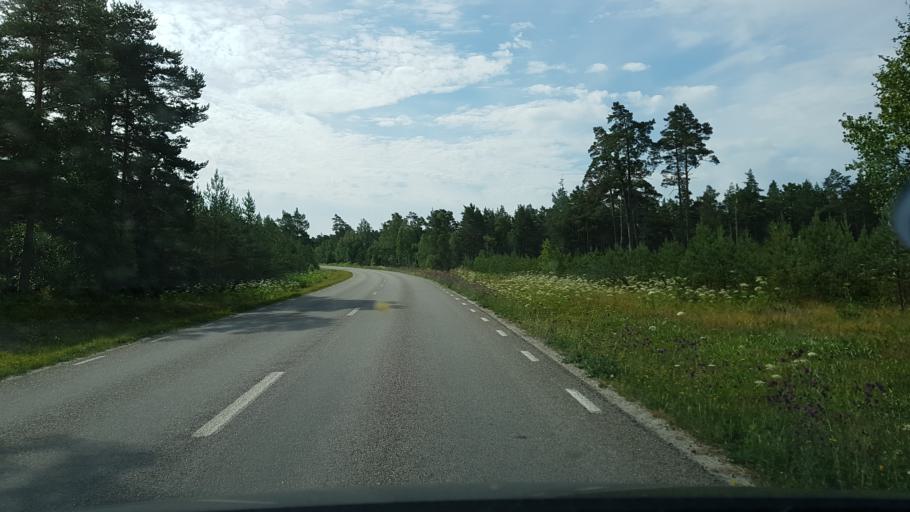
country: SE
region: Gotland
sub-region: Gotland
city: Hemse
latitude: 57.4545
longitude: 18.5785
